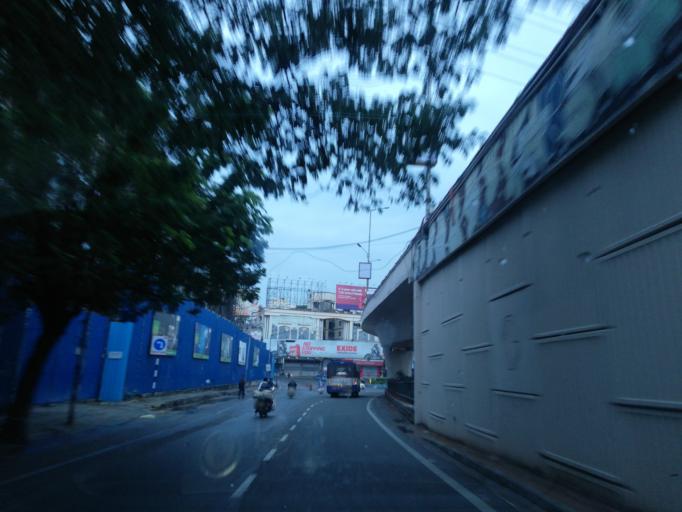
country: IN
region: Telangana
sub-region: Hyderabad
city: Hyderabad
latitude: 17.4248
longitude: 78.4483
